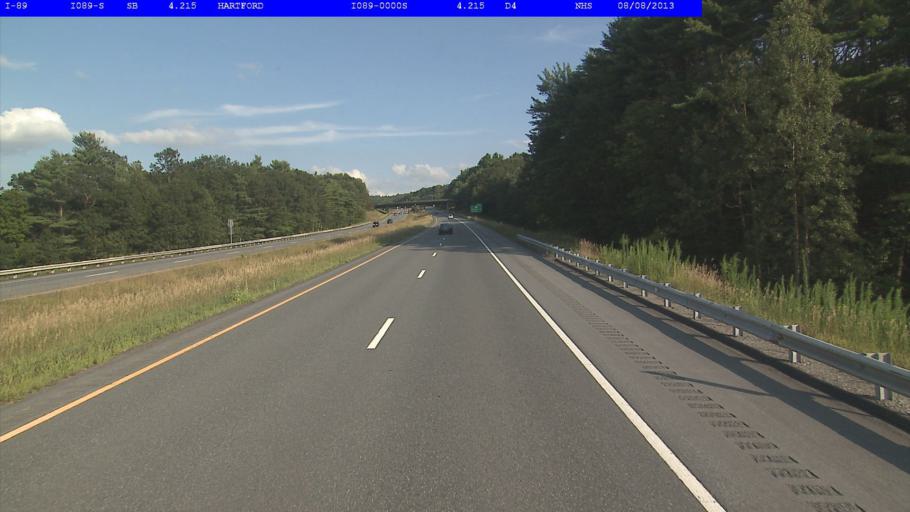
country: US
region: Vermont
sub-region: Windsor County
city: White River Junction
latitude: 43.6698
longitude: -72.3895
